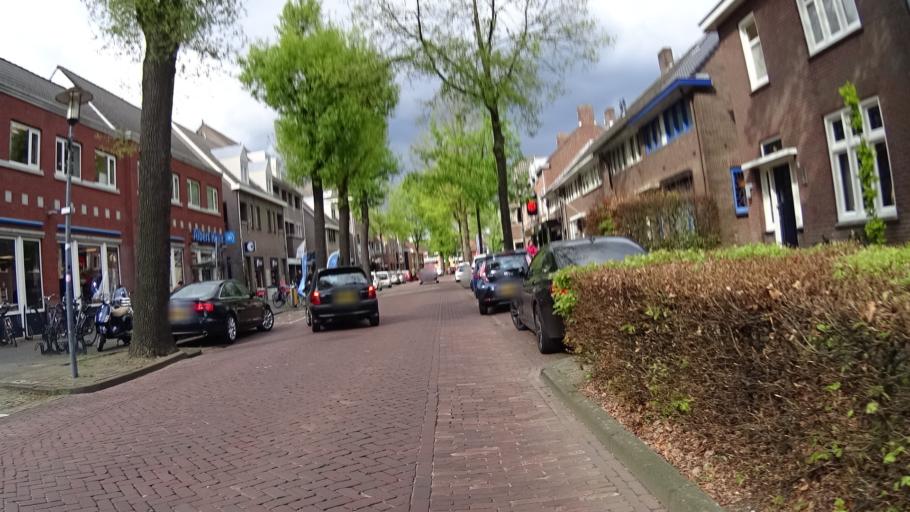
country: NL
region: North Brabant
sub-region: Gemeente Nuenen, Gerwen en Nederwetten
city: Nuenen
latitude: 51.4721
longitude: 5.5458
